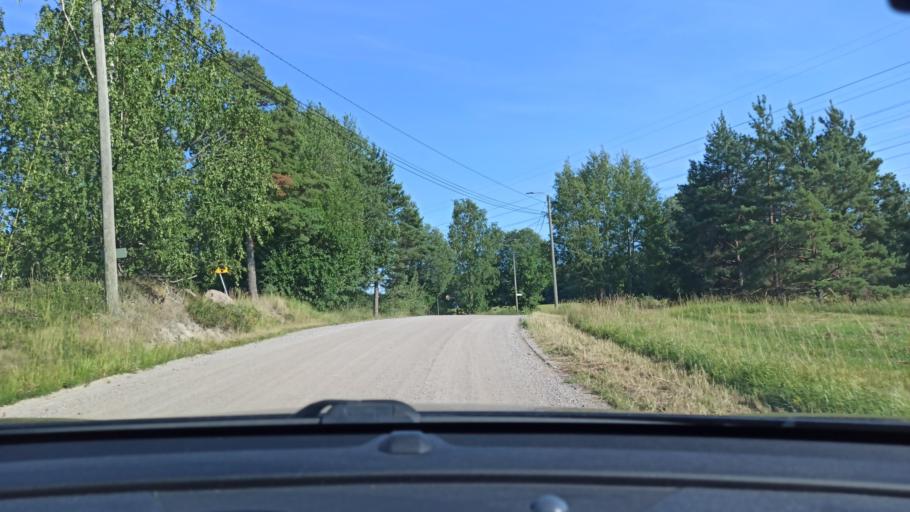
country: FI
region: Uusimaa
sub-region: Helsinki
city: Espoo
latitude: 60.2062
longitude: 24.5580
